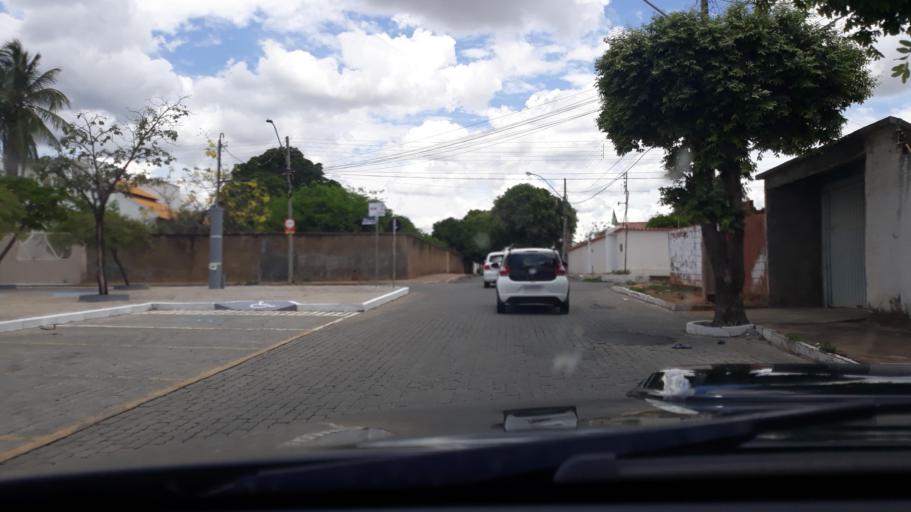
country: BR
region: Bahia
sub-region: Guanambi
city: Guanambi
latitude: -14.2255
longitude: -42.7728
